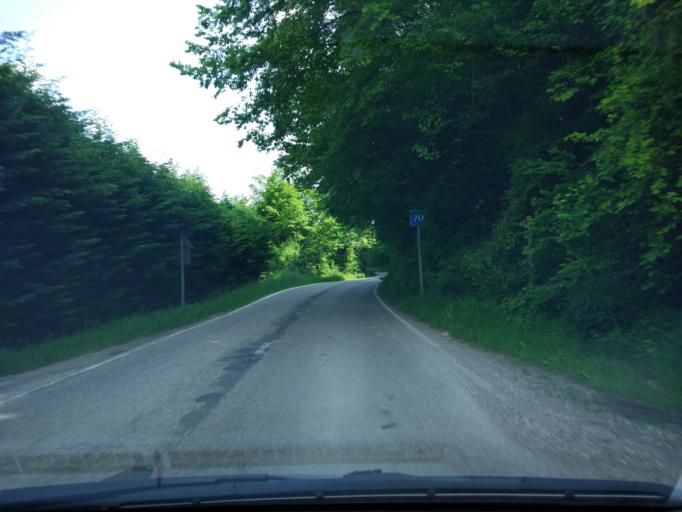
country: IT
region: Veneto
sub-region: Provincia di Verona
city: Selva di Progno
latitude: 45.6042
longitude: 11.1428
